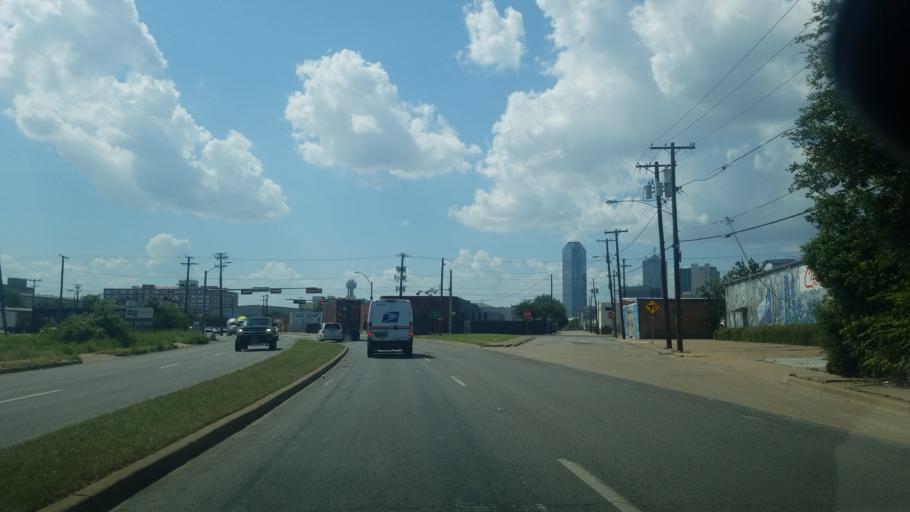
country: US
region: Texas
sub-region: Dallas County
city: Dallas
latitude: 32.7647
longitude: -96.7883
